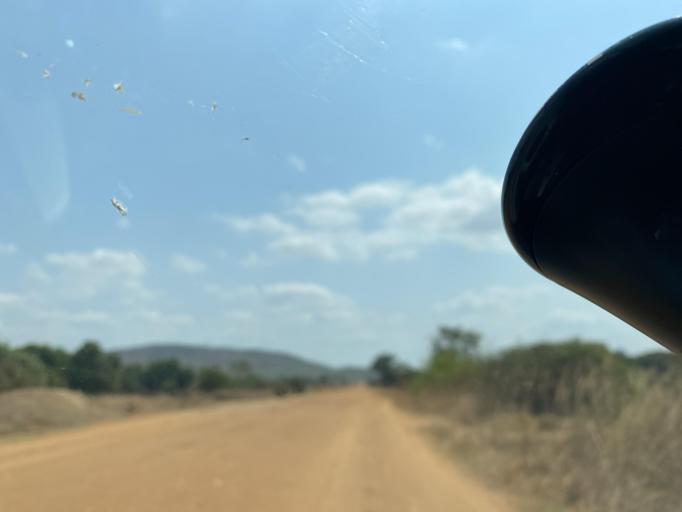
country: ZM
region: Lusaka
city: Chongwe
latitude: -15.5939
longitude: 28.7567
